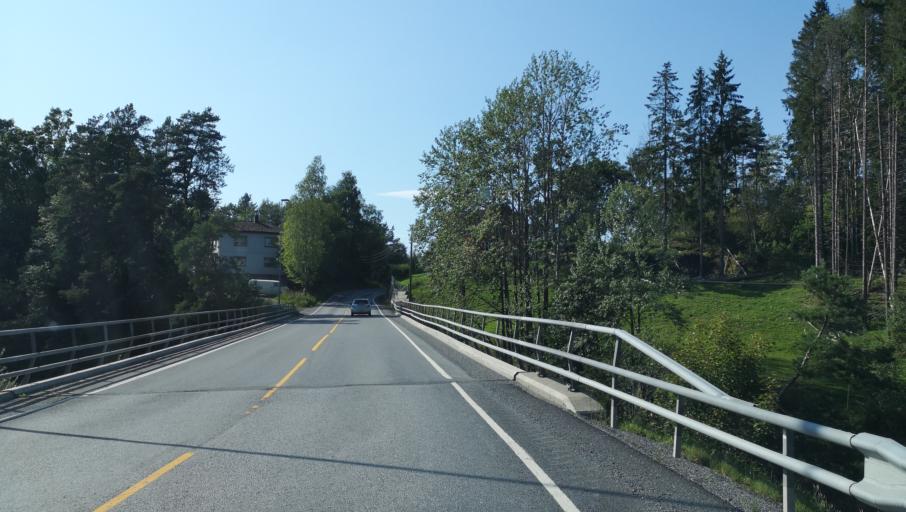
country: NO
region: Ostfold
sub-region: Valer
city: Kirkebygda
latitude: 59.5482
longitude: 10.8463
